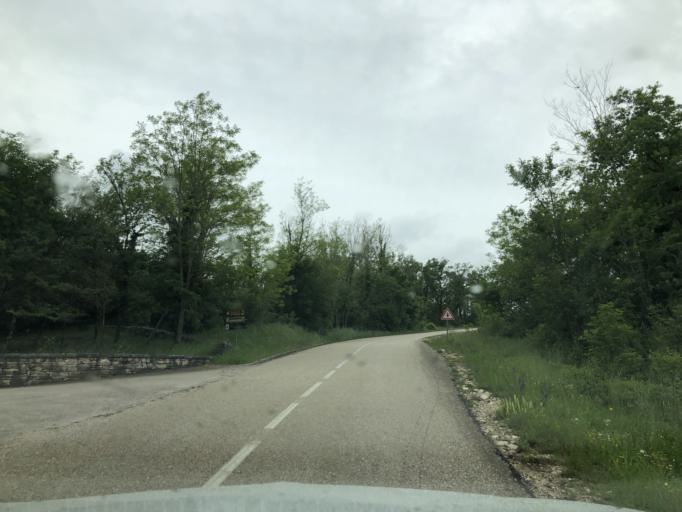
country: HR
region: Istarska
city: Buje
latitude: 45.4312
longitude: 13.6984
